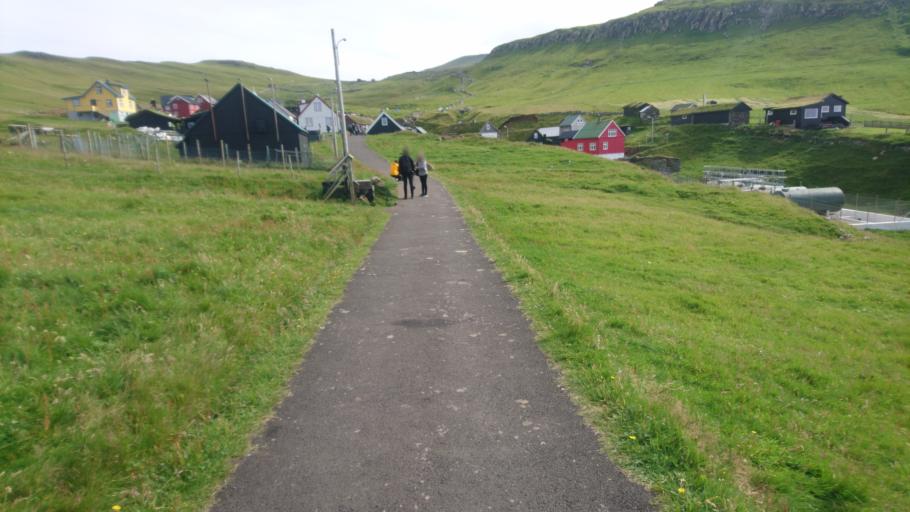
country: FO
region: Vagar
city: Sorvagur
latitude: 62.1027
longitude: -7.6472
